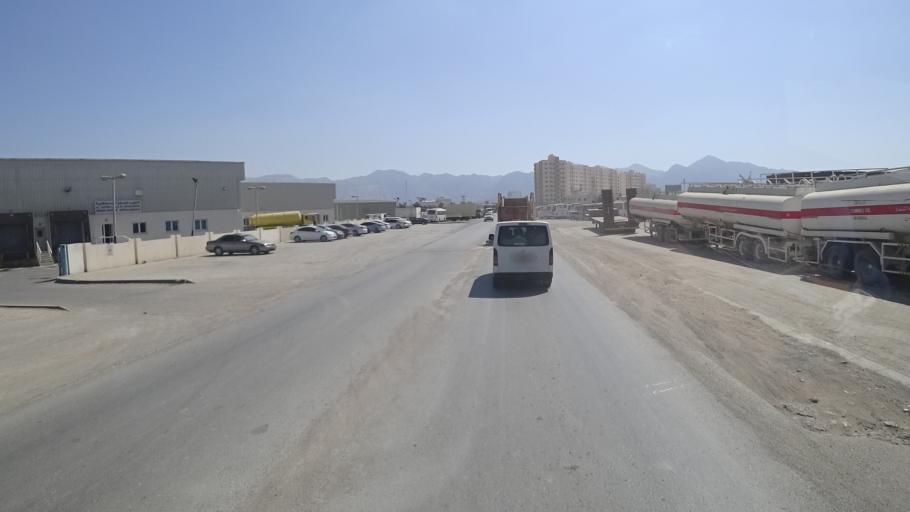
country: OM
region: Muhafazat Masqat
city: Bawshar
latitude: 23.5794
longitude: 58.3647
